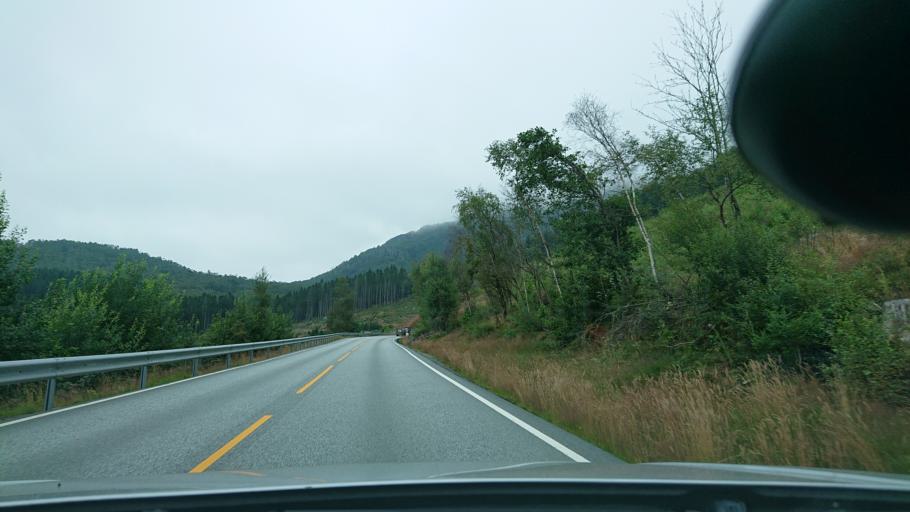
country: NO
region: Rogaland
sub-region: Hjelmeland
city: Hjelmelandsvagen
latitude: 59.1769
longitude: 6.1441
